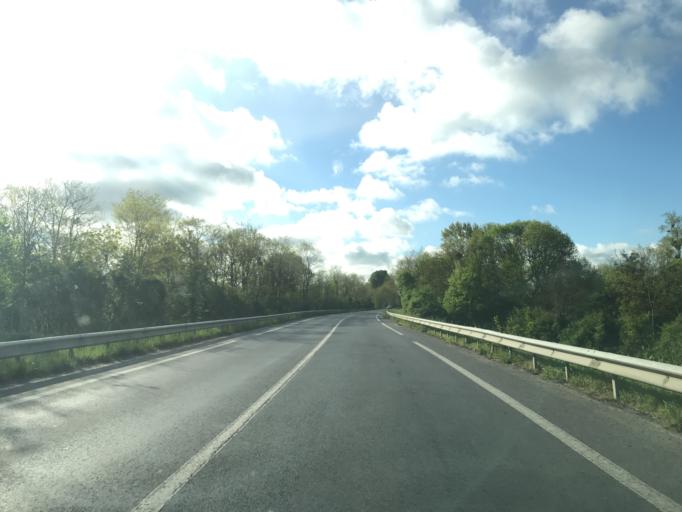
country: FR
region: Lower Normandy
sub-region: Departement du Calvados
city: Dozule
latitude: 49.2271
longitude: -0.0827
